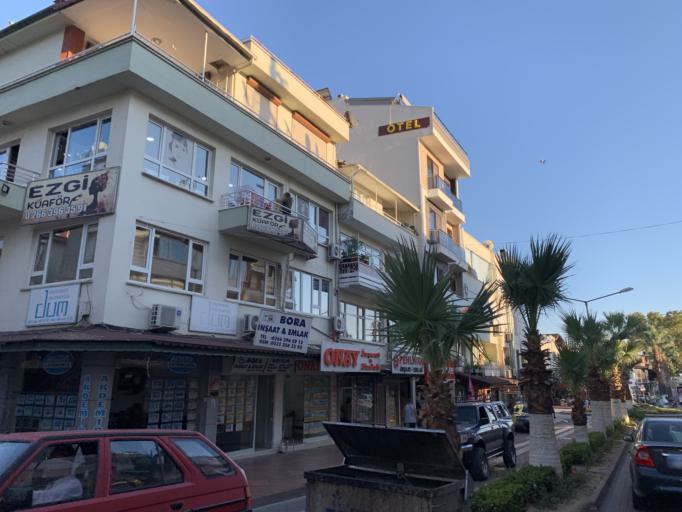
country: TR
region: Balikesir
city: Altinoluk
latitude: 39.5680
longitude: 26.7446
